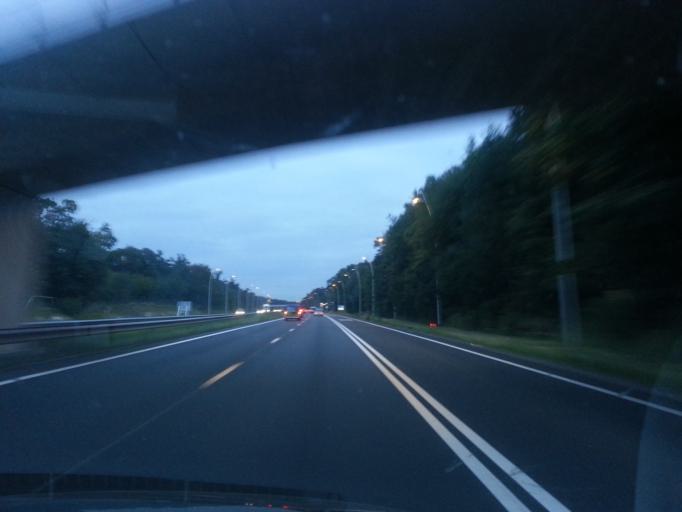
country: NL
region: North Brabant
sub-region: Gemeente Loon op Zand
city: Loon op Zand
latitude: 51.6455
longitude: 5.0582
